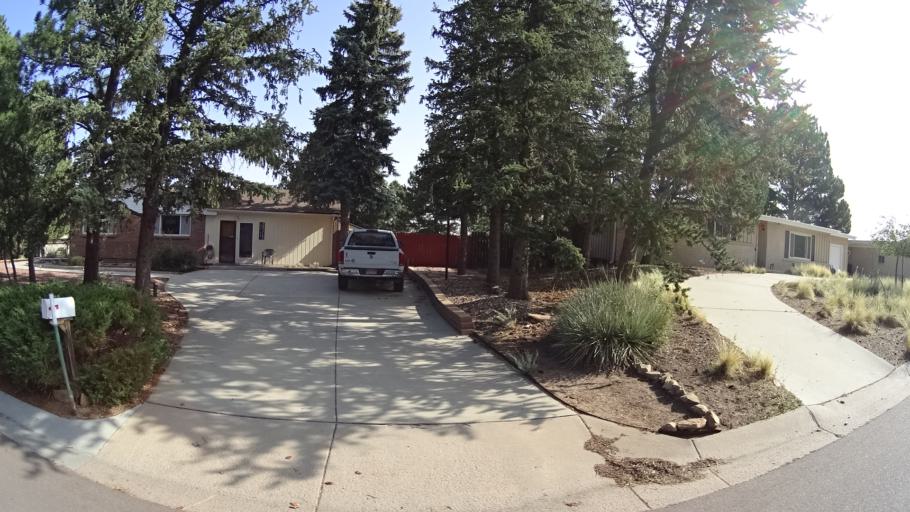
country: US
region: Colorado
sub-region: El Paso County
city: Colorado Springs
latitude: 38.8149
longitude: -104.8616
